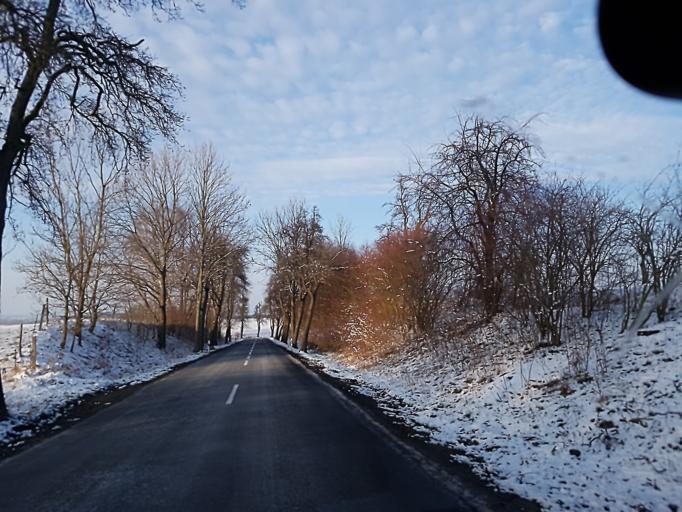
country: DE
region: Saxony
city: Mugeln
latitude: 51.2050
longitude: 13.0844
